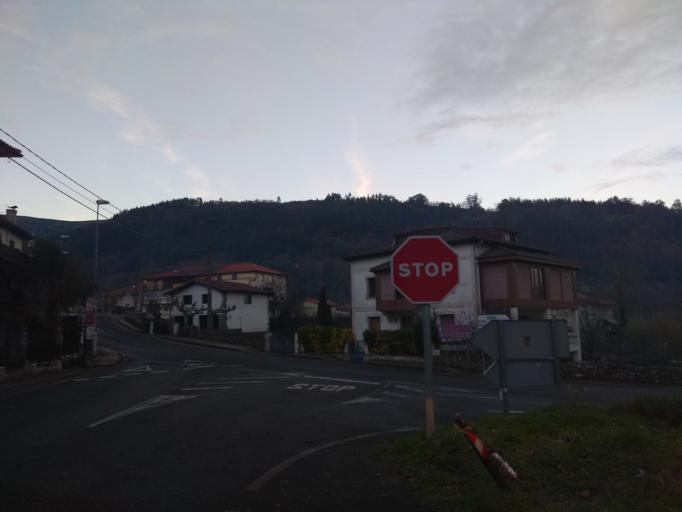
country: ES
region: Cantabria
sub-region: Provincia de Cantabria
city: Arredondo
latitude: 43.2731
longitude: -3.5983
